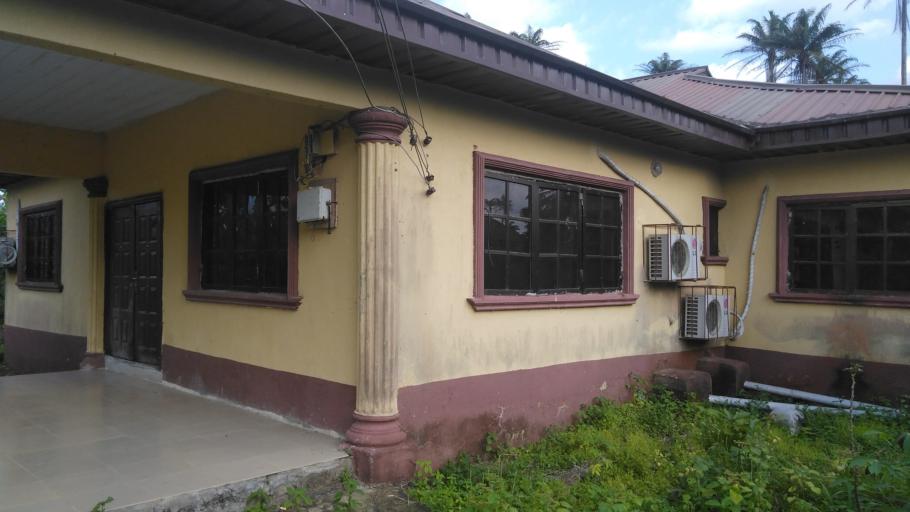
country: NG
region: Edo
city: Siluko
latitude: 6.1417
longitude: 5.2031
